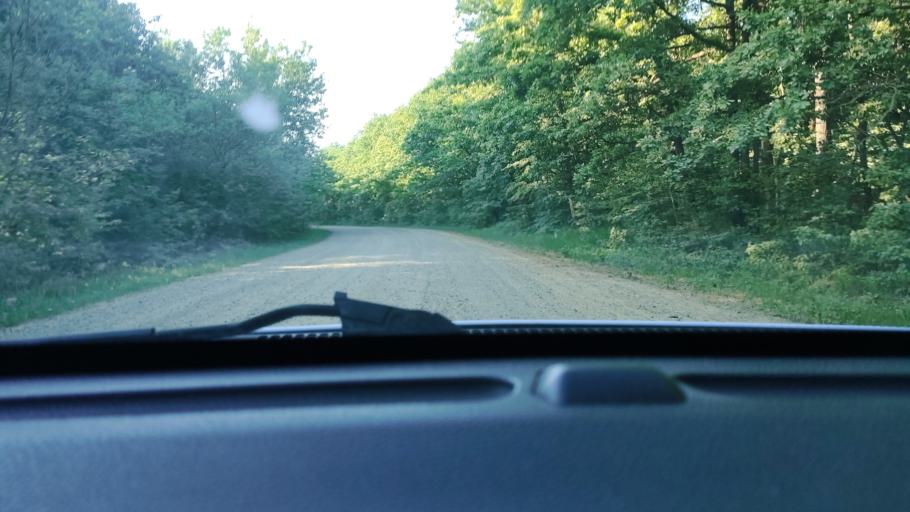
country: RU
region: Krasnodarskiy
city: Goryachiy Klyuch
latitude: 44.7092
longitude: 38.9924
